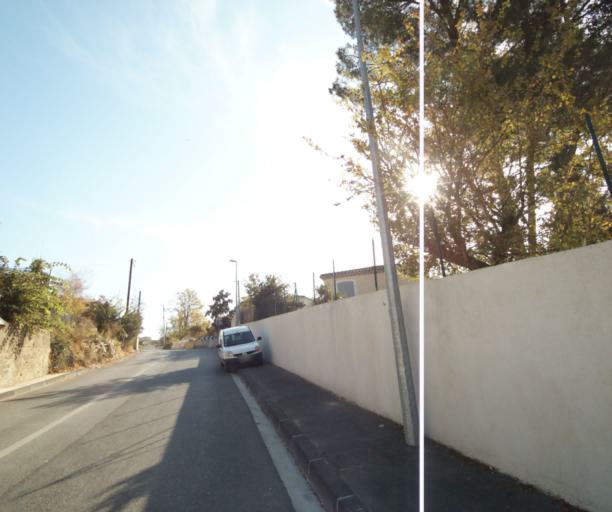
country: FR
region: Provence-Alpes-Cote d'Azur
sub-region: Departement des Bouches-du-Rhone
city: La Penne-sur-Huveaune
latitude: 43.3098
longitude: 5.5009
